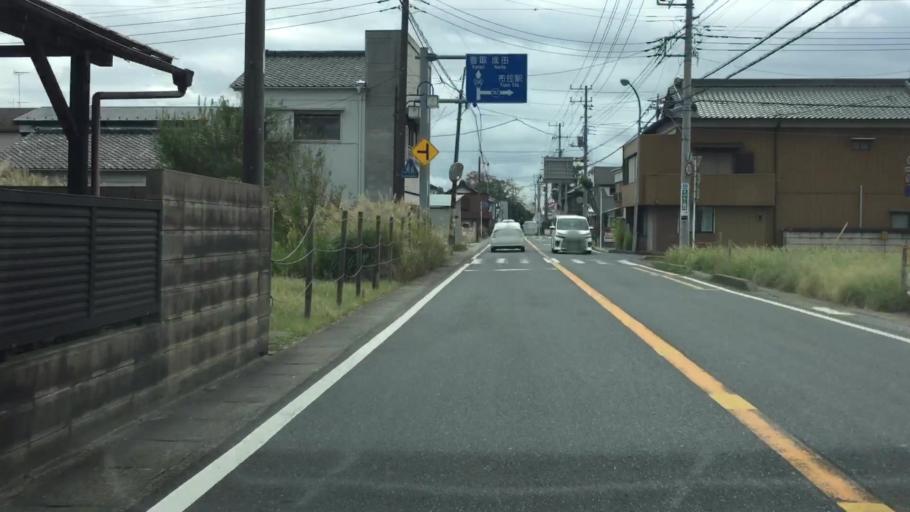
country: JP
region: Ibaraki
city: Ryugasaki
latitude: 35.8532
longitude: 140.1372
